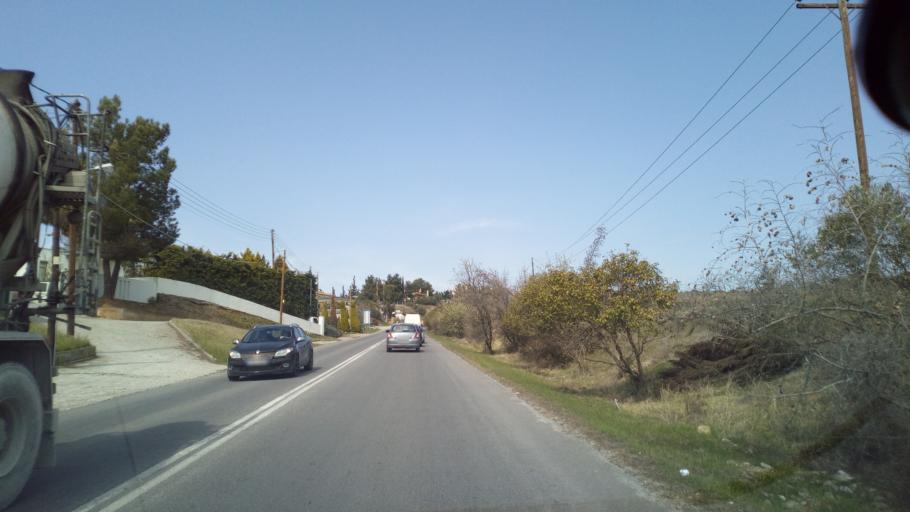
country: GR
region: Central Macedonia
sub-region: Nomos Thessalonikis
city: Thermi
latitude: 40.5666
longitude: 23.0250
